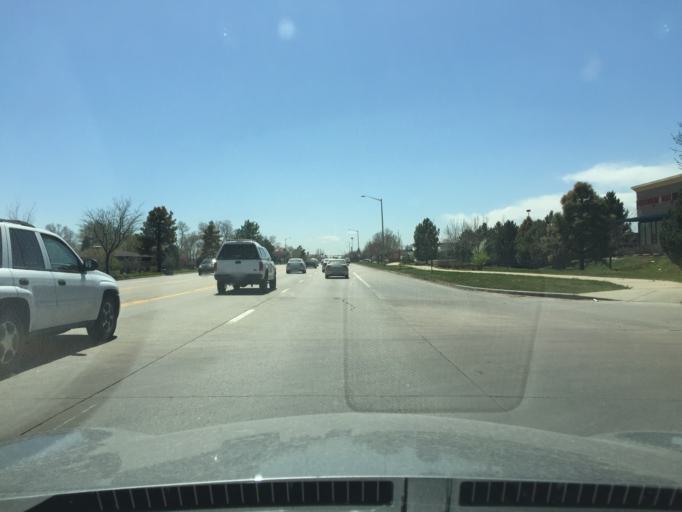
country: US
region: Colorado
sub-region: Boulder County
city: Longmont
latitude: 40.1561
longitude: -105.1308
